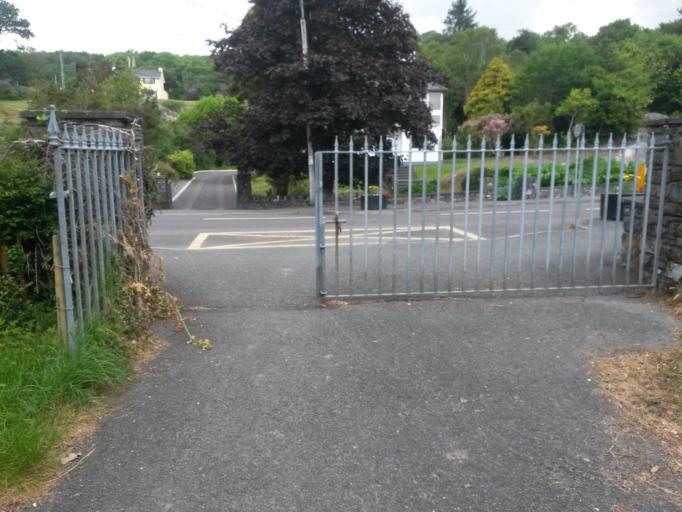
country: IE
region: Munster
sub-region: County Cork
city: Bantry
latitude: 51.7502
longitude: -9.5460
